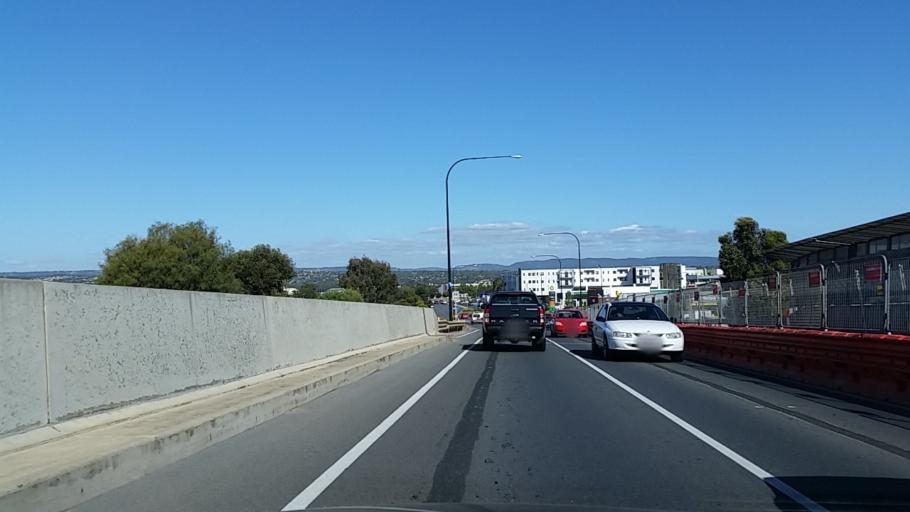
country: AU
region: South Australia
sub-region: Salisbury
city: Ingle Farm
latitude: -34.8039
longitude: 138.6133
